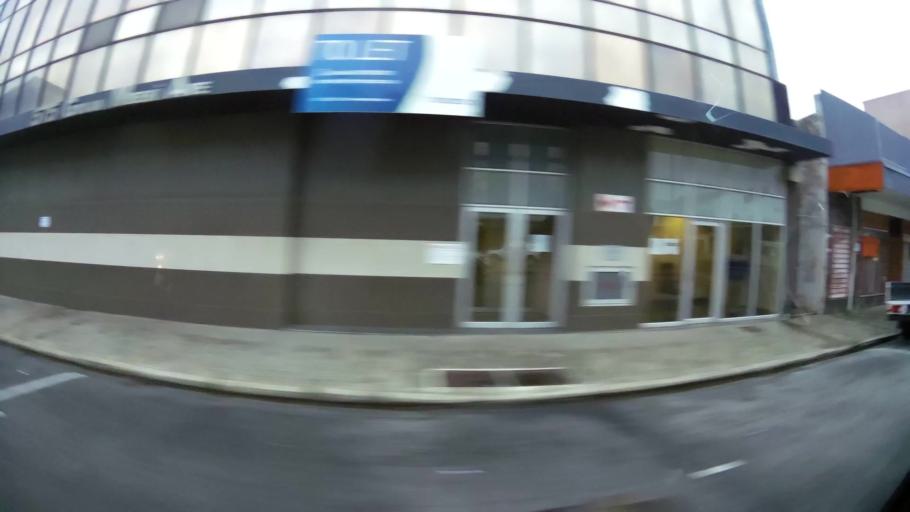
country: ZA
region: Eastern Cape
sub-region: Nelson Mandela Bay Metropolitan Municipality
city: Port Elizabeth
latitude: -33.9454
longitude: 25.6063
